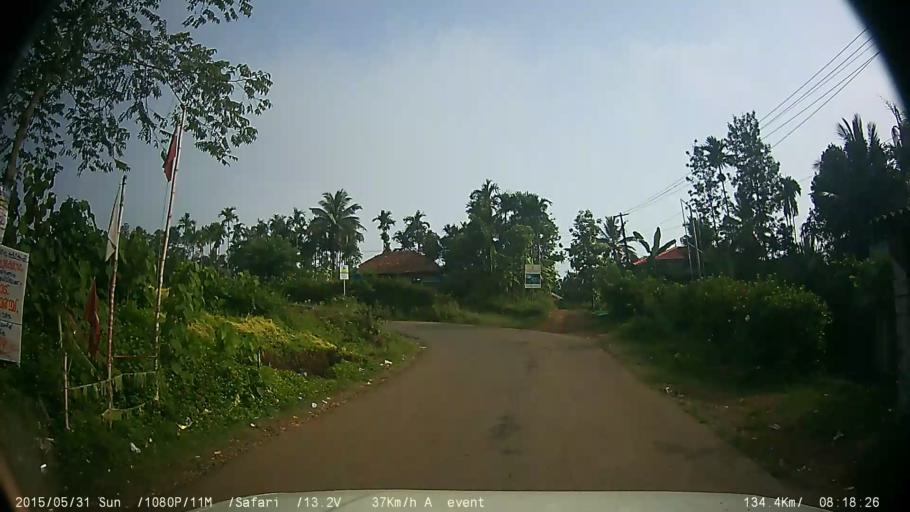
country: IN
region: Kerala
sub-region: Wayanad
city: Kalpetta
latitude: 11.6661
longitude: 75.9874
